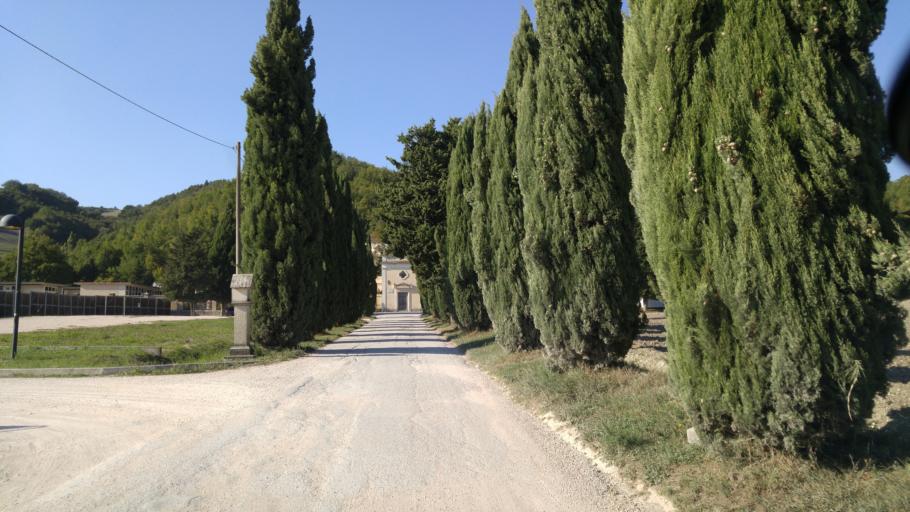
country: IT
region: The Marches
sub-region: Provincia di Pesaro e Urbino
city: Fermignano
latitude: 43.6718
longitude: 12.6344
